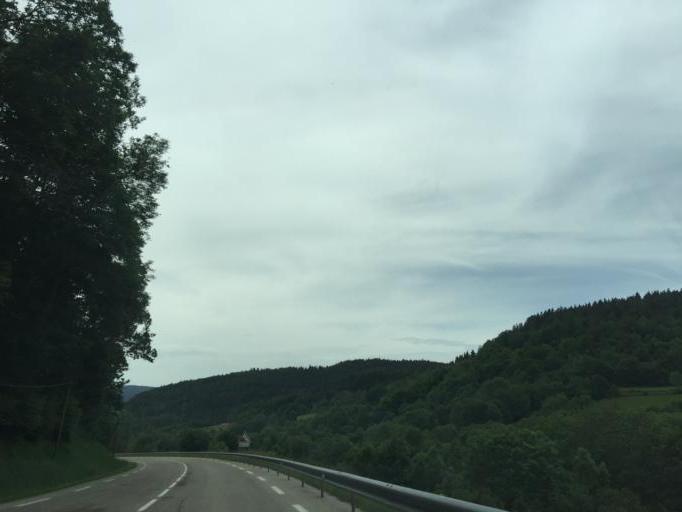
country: FR
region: Rhone-Alpes
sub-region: Departement de la Loire
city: Bourg-Argental
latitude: 45.3235
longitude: 4.5226
